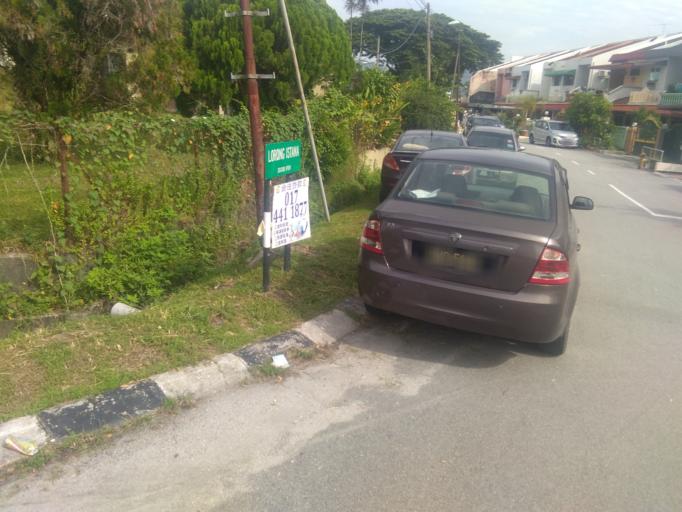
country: MY
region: Perak
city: Ipoh
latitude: 4.6053
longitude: 101.0814
